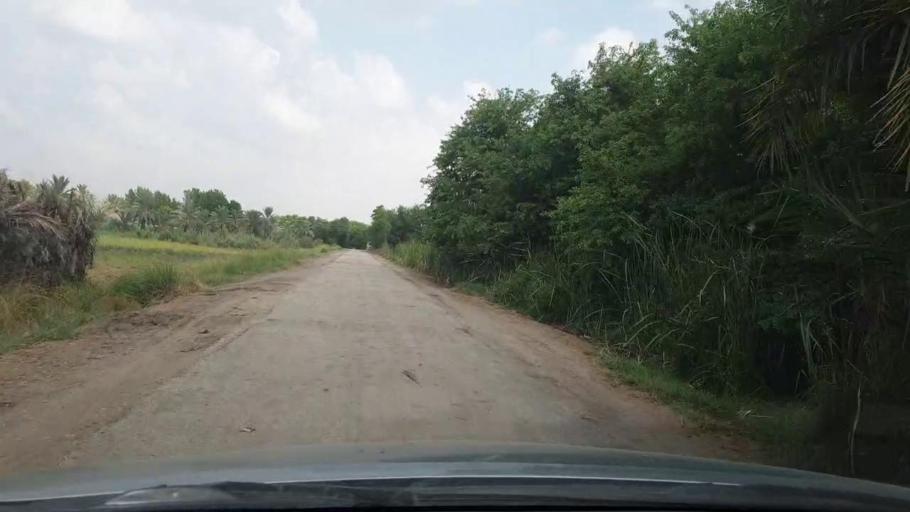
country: PK
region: Sindh
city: Khairpur
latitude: 27.4660
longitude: 68.7677
